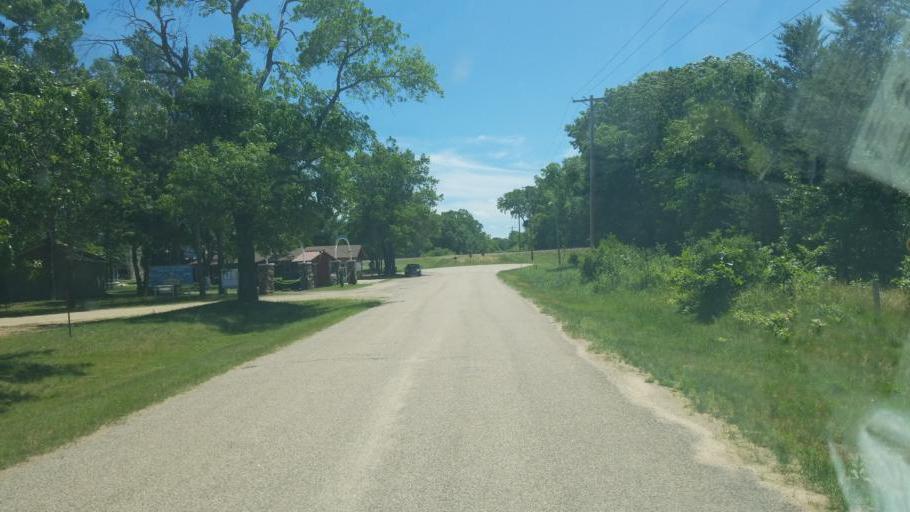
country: US
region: Wisconsin
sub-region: Juneau County
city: New Lisbon
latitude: 44.0214
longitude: -90.0578
